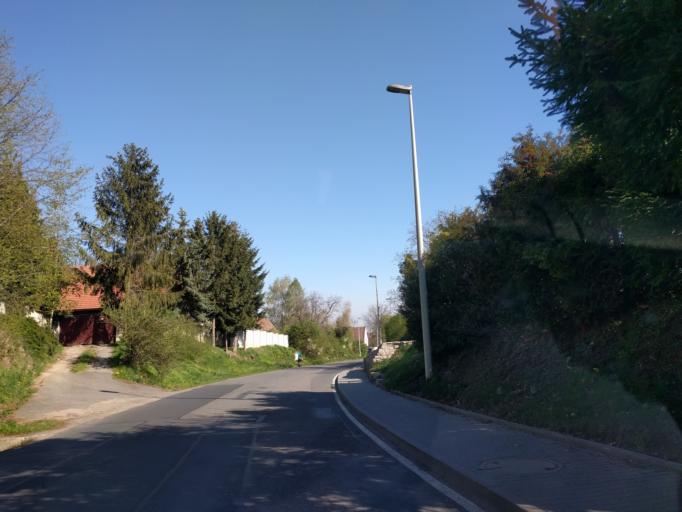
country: CZ
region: Central Bohemia
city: Mukarov
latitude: 50.0210
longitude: 14.7879
